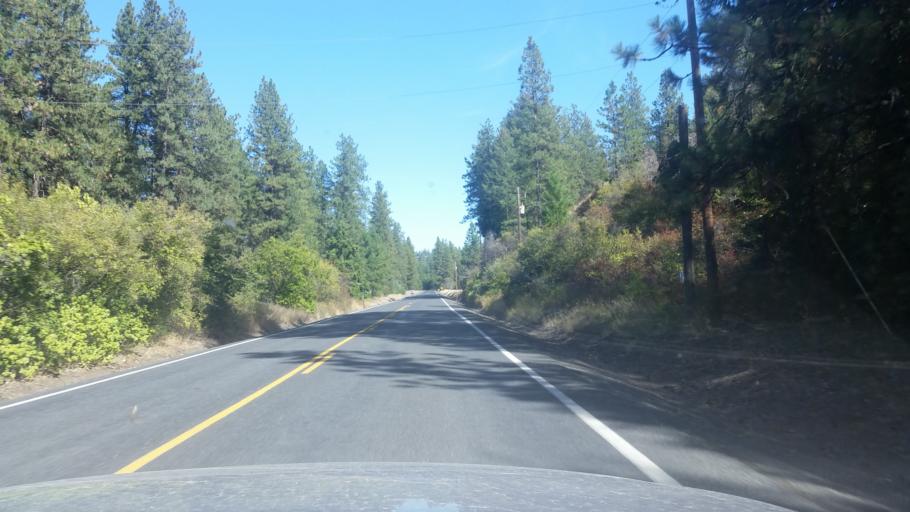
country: US
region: Washington
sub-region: Spokane County
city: Spokane
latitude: 47.5697
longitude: -117.4825
